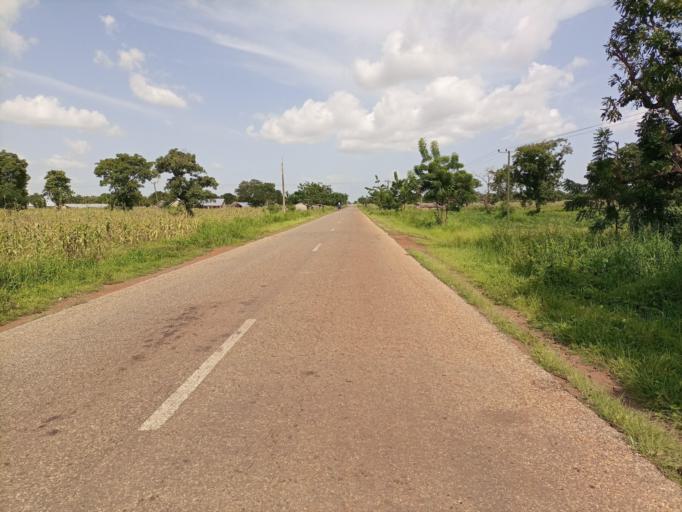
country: GH
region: Northern
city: Savelugu
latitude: 9.5734
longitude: -1.0096
